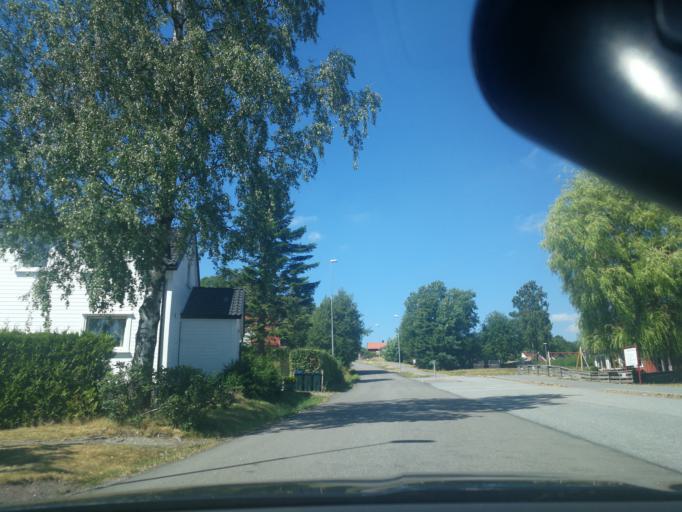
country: NO
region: Vestfold
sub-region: Stokke
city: Melsomvik
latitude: 59.2312
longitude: 10.3391
